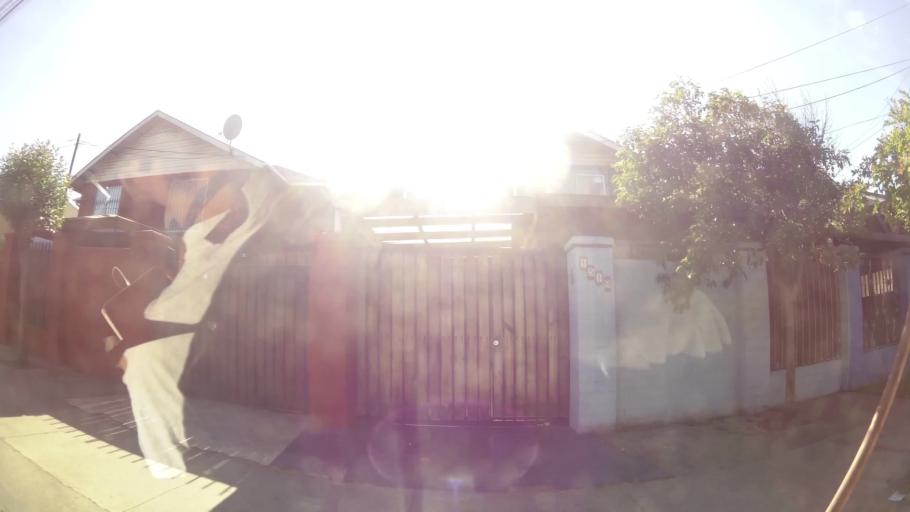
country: CL
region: Santiago Metropolitan
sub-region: Provincia de Maipo
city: San Bernardo
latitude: -33.6088
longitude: -70.6943
